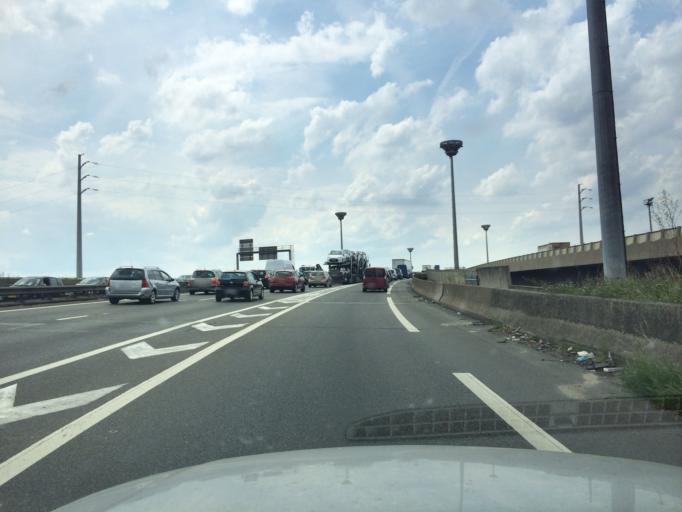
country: FR
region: Ile-de-France
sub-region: Departement du Val-de-Marne
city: Choisy-le-Roi
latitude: 48.7767
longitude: 2.4374
